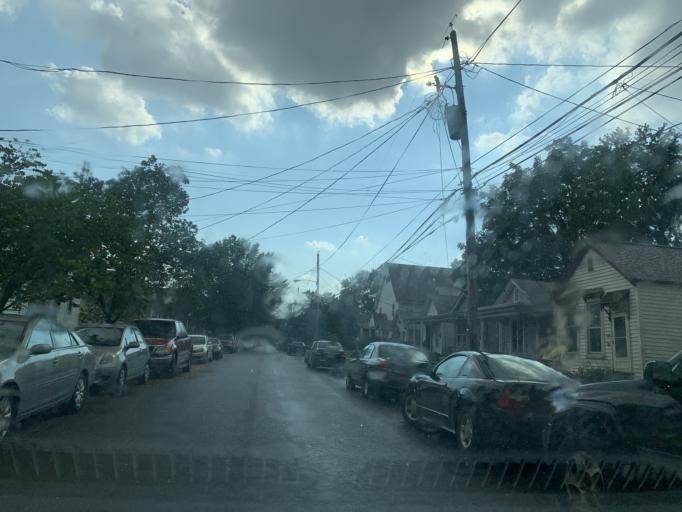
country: US
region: Kentucky
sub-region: Jefferson County
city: Audubon Park
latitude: 38.2164
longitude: -85.7466
